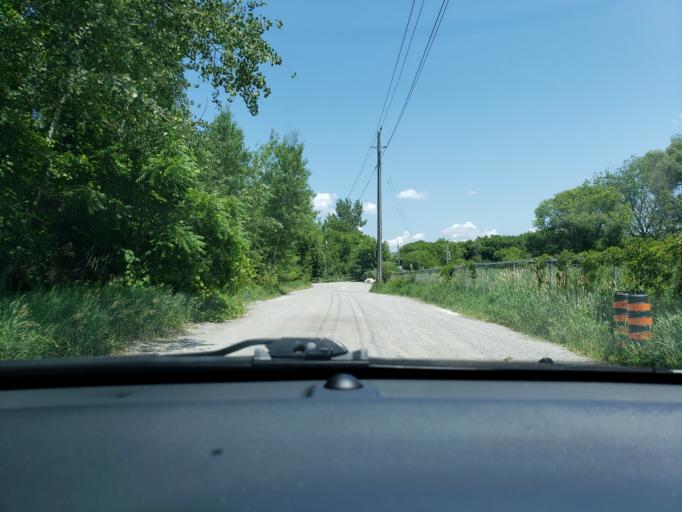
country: CA
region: Ontario
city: Newmarket
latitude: 44.0688
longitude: -79.4584
